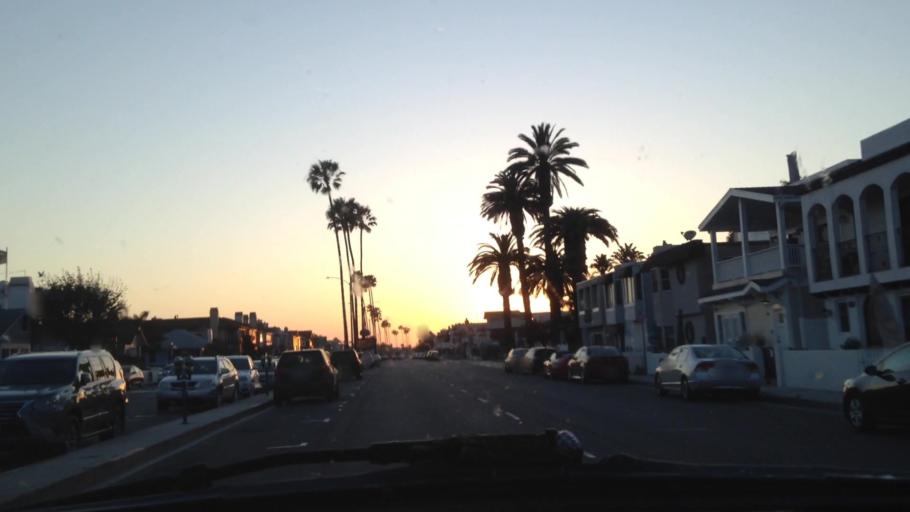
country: US
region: California
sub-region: Orange County
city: Newport Beach
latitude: 33.6038
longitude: -117.9052
